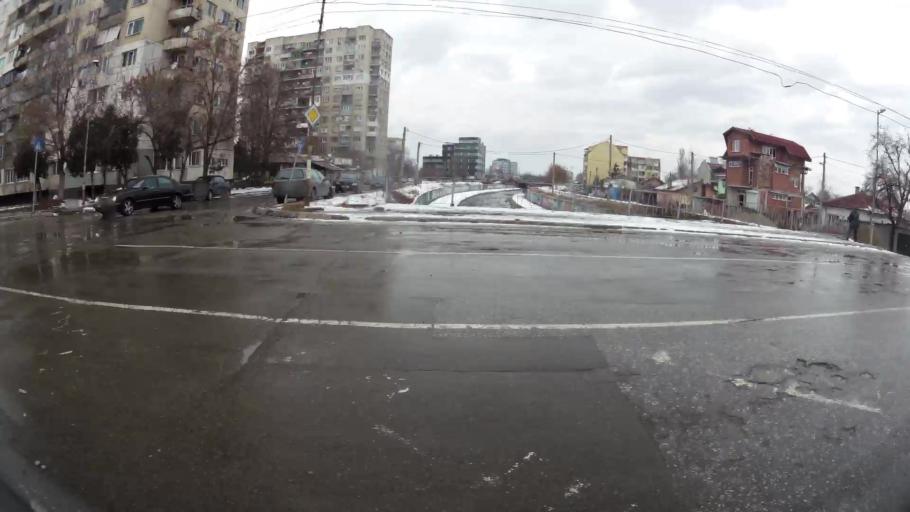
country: BG
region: Sofia-Capital
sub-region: Stolichna Obshtina
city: Sofia
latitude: 42.7059
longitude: 23.3706
